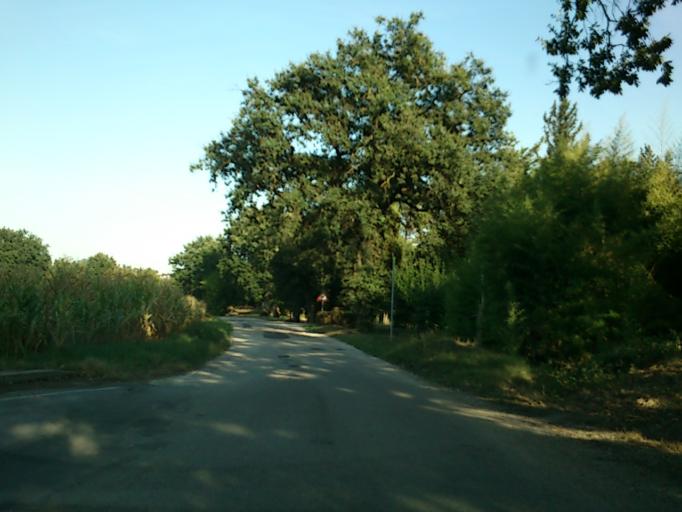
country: IT
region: The Marches
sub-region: Provincia di Pesaro e Urbino
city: Saltara
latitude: 43.7373
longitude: 12.9030
